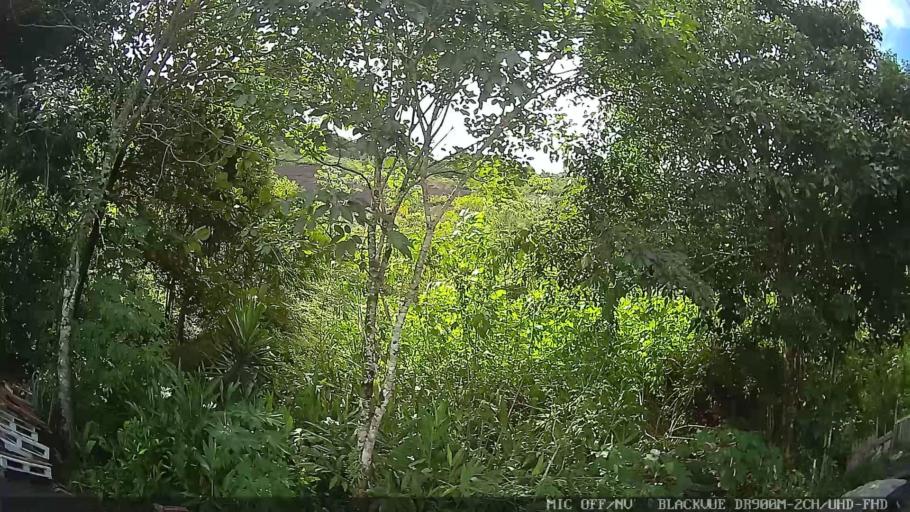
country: BR
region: Sao Paulo
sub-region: Caraguatatuba
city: Caraguatatuba
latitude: -23.6242
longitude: -45.4406
